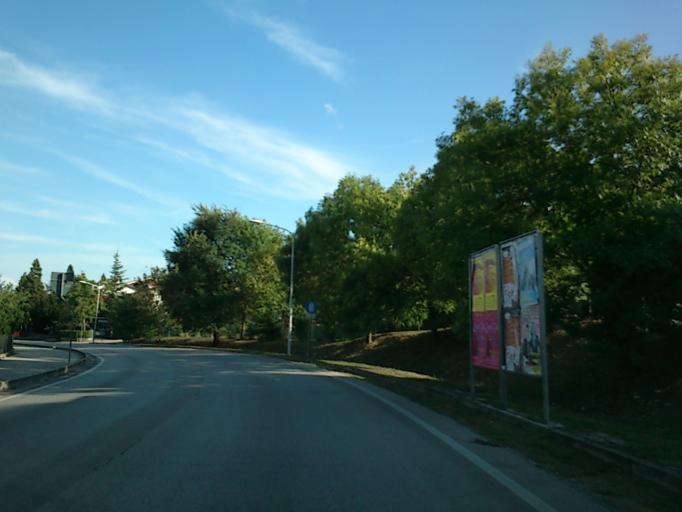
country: IT
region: The Marches
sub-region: Provincia di Pesaro e Urbino
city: Urbania
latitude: 43.6730
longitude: 12.5114
